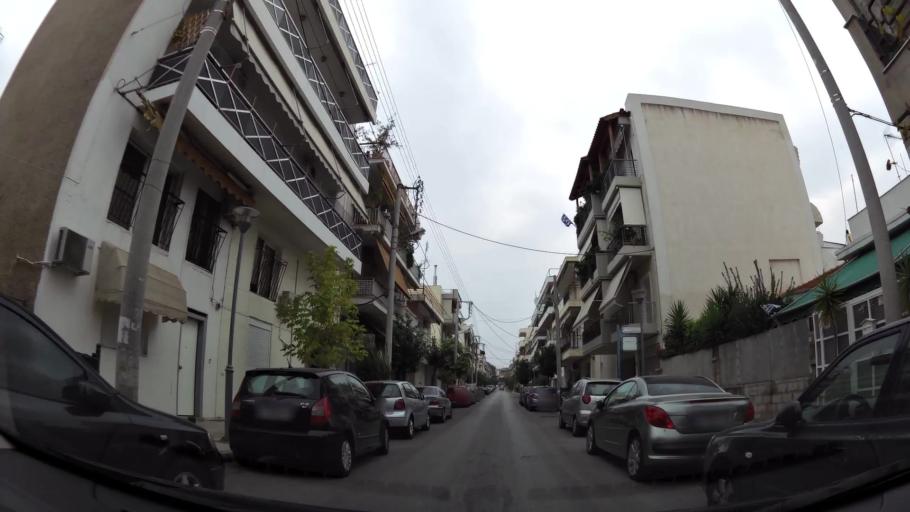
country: GR
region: Attica
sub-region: Nomarchia Athinas
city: Aigaleo
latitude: 37.9946
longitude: 23.6883
